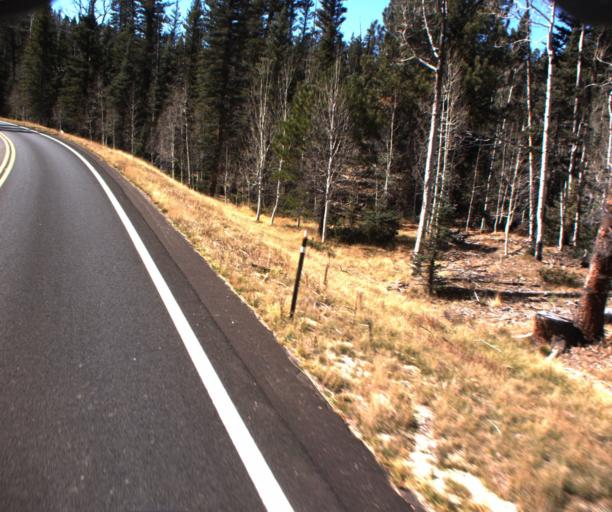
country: US
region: Arizona
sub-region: Coconino County
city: Grand Canyon
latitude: 36.4527
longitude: -112.1344
